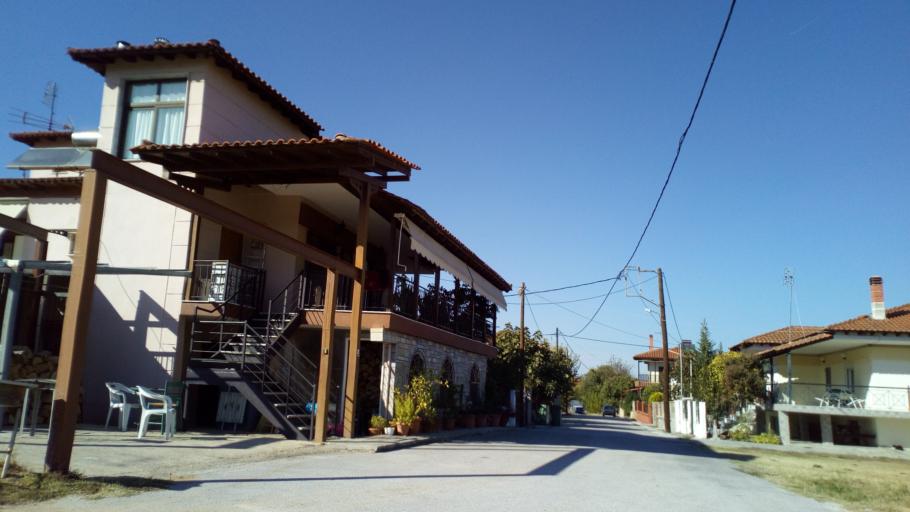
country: GR
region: Central Macedonia
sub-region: Nomos Thessalonikis
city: Gerakarou
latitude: 40.6341
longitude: 23.2472
